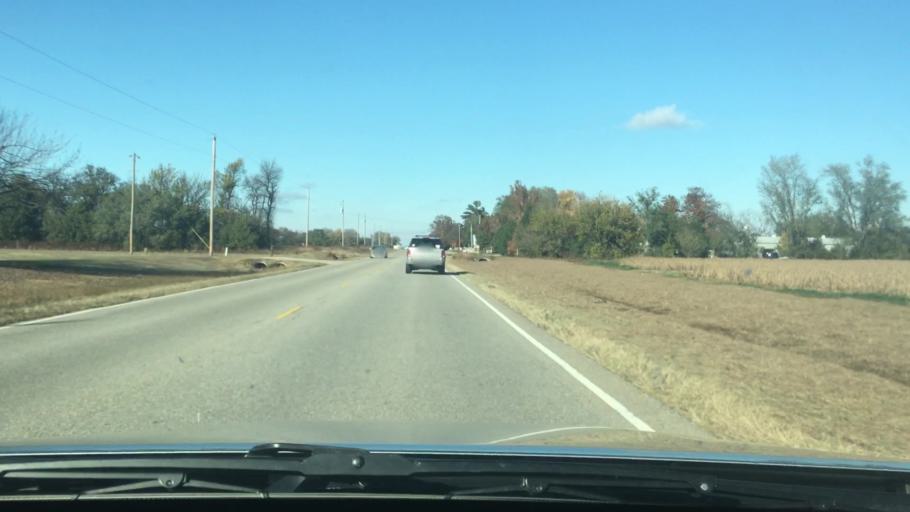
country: US
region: Kansas
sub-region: Sedgwick County
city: Maize
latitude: 37.7607
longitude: -97.4808
